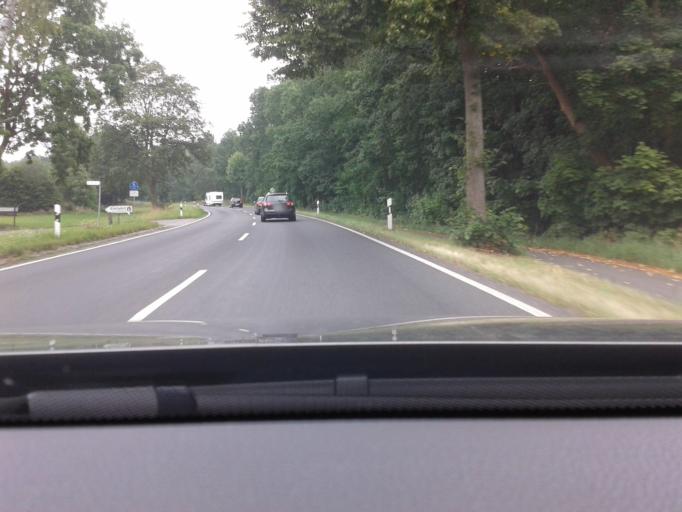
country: DE
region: Lower Saxony
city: Leiferde
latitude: 52.4788
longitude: 10.4661
